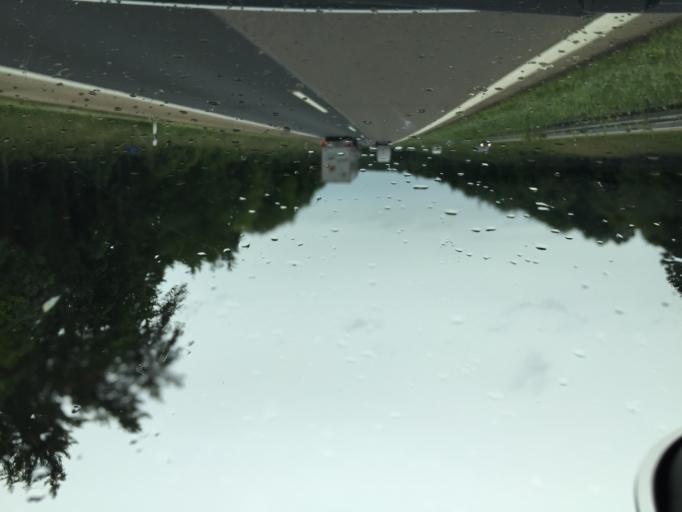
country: DE
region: Bavaria
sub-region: Regierungsbezirk Unterfranken
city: Oberthulba
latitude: 50.1776
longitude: 9.9583
